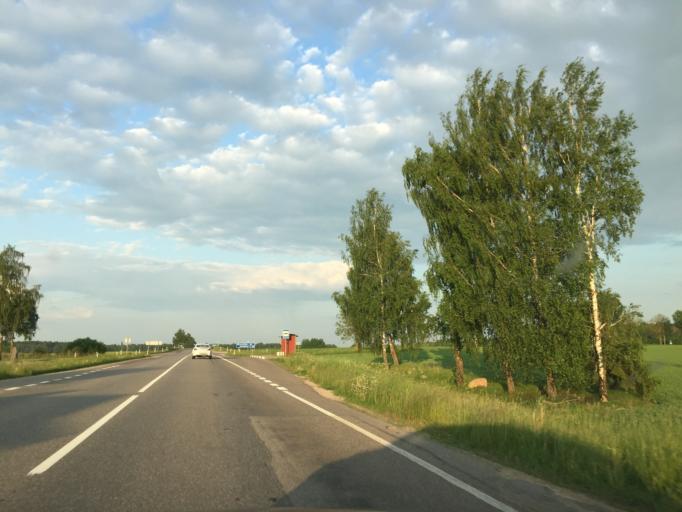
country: LT
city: Venta
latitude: 56.0052
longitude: 22.7219
